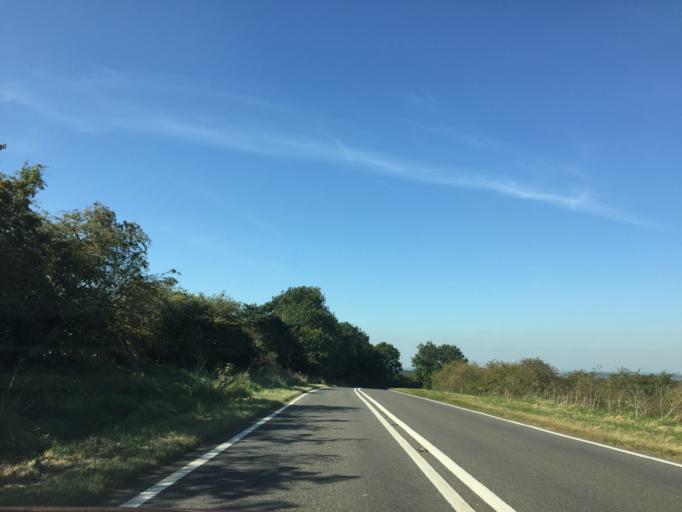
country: GB
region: England
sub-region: Leicestershire
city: Houghton on the Hill
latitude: 52.6493
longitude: -0.9063
